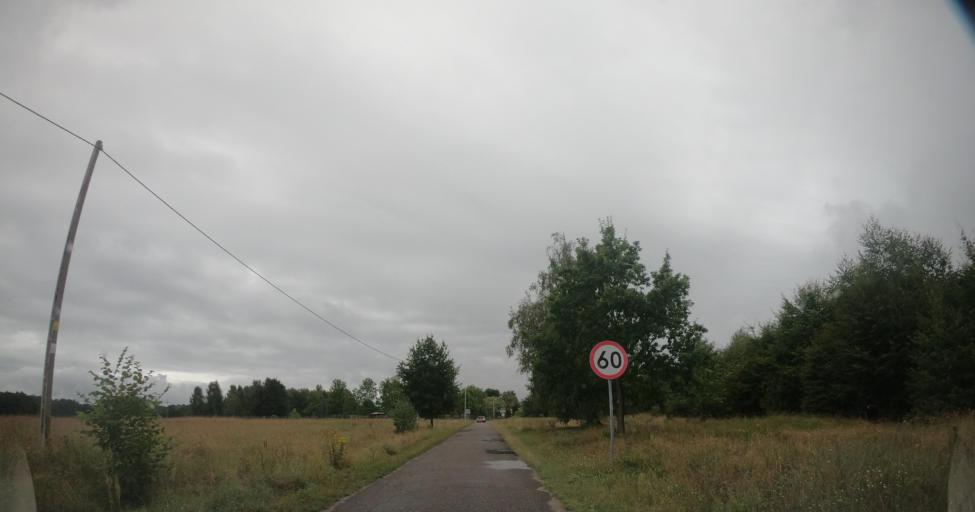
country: PL
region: West Pomeranian Voivodeship
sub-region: Powiat lobeski
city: Wegorzyno
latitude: 53.5269
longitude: 15.4976
